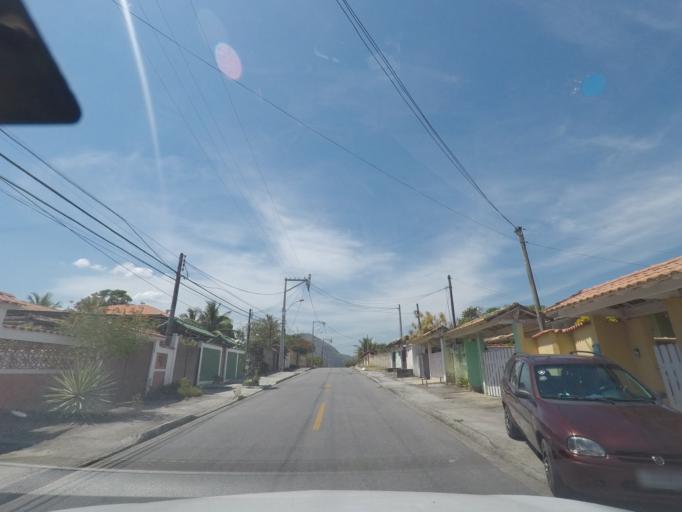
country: BR
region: Rio de Janeiro
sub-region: Marica
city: Marica
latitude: -22.9668
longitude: -42.9585
